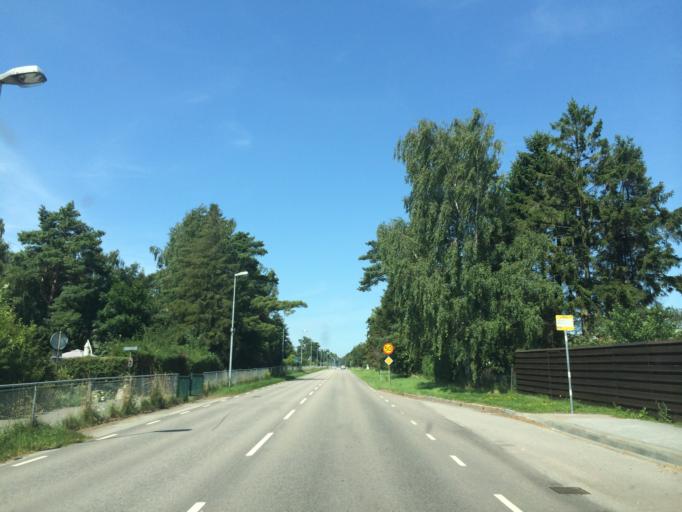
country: SE
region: Skane
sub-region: Vellinge Kommun
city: Hollviken
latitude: 55.4095
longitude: 12.9797
